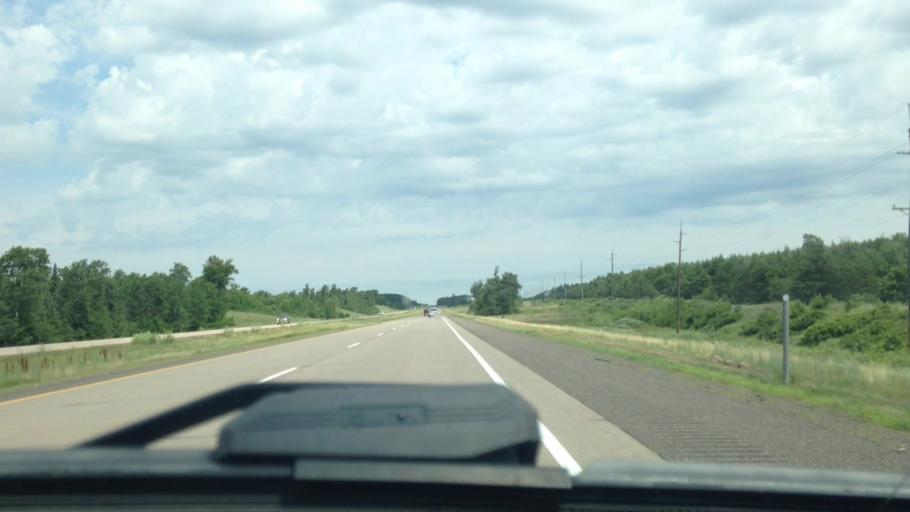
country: US
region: Wisconsin
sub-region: Douglas County
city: Lake Nebagamon
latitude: 46.1893
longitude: -91.7990
